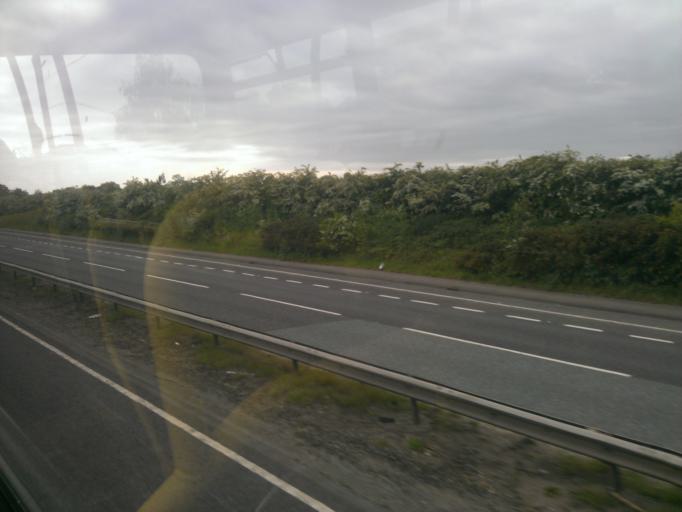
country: GB
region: England
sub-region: Suffolk
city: East Bergholt
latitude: 51.9433
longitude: 0.9558
